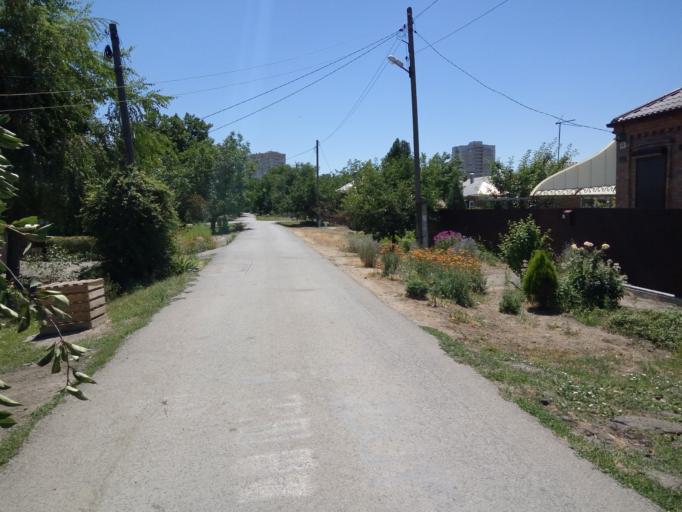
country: RU
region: Rostov
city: Bataysk
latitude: 47.1424
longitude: 39.7709
